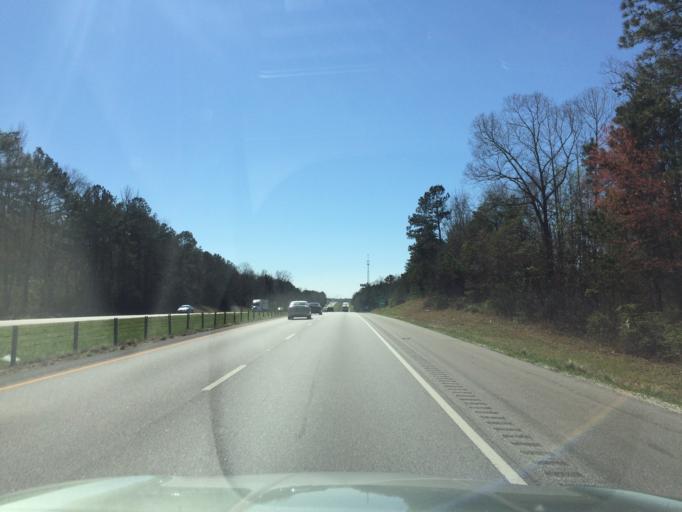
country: US
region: Alabama
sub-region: Lee County
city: Auburn
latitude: 32.5691
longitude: -85.4881
